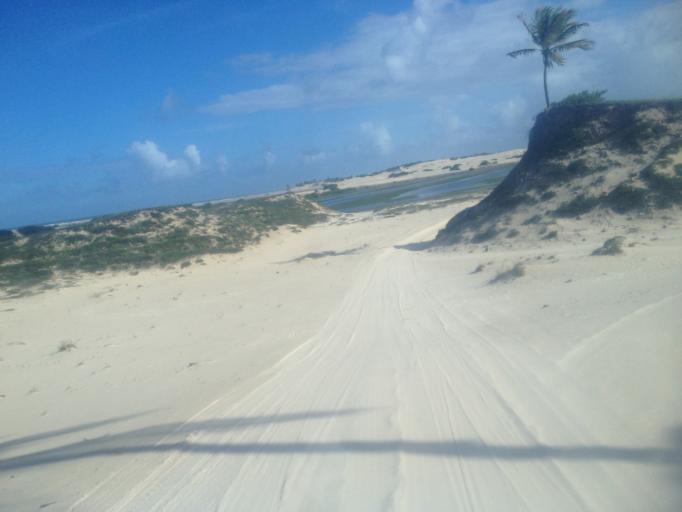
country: BR
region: Sergipe
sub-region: Indiaroba
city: Indiaroba
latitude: -11.4707
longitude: -37.3681
